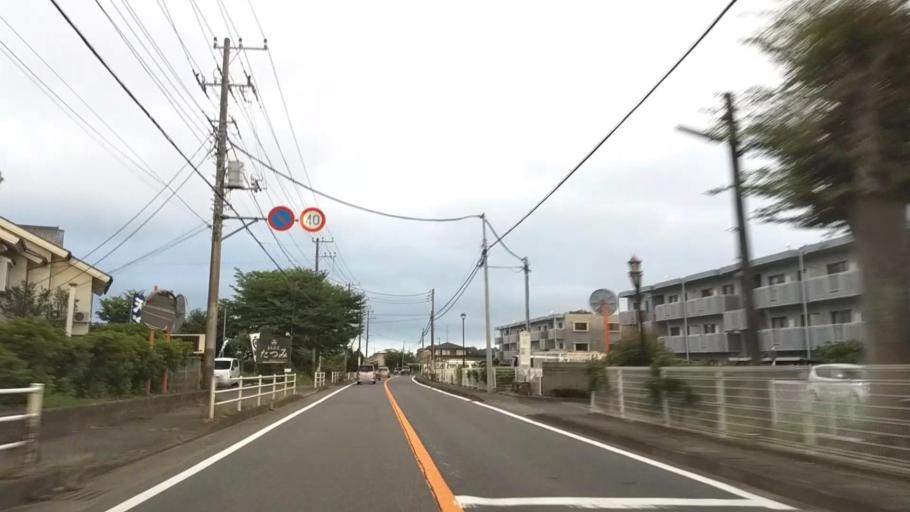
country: JP
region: Kanagawa
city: Atsugi
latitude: 35.4696
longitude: 139.3268
